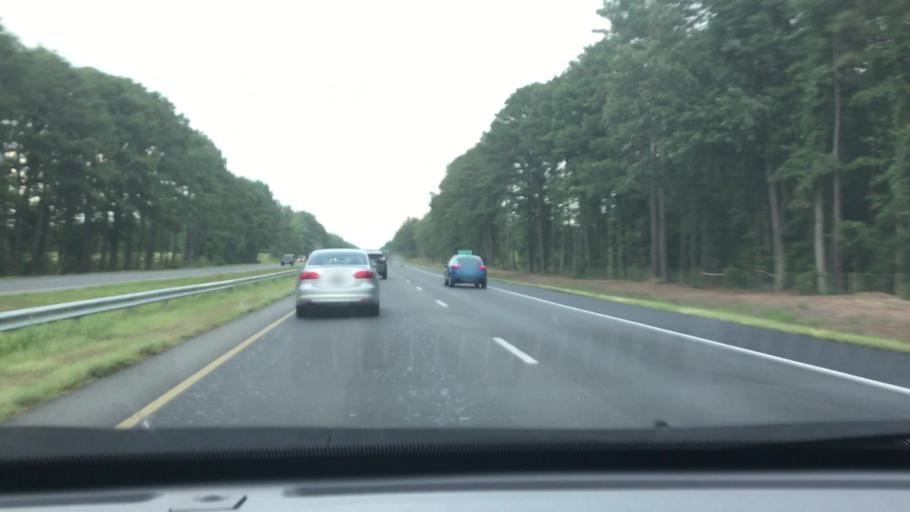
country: US
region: North Carolina
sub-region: Cumberland County
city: Eastover
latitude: 35.1381
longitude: -78.7384
